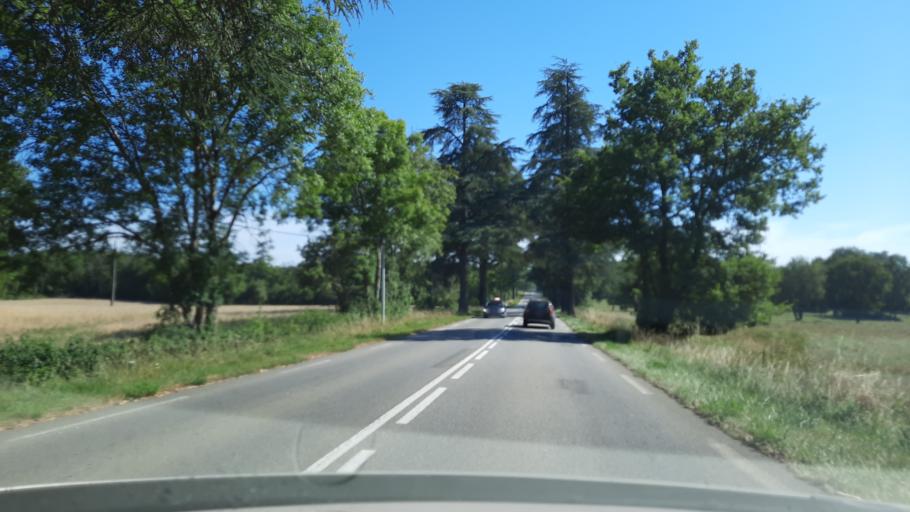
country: FR
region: Midi-Pyrenees
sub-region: Departement du Tarn-et-Garonne
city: Caylus
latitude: 44.3009
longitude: 1.8764
